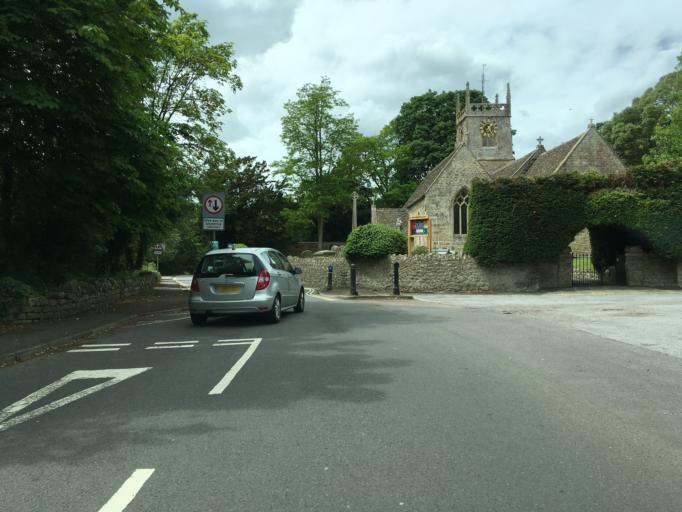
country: GB
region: England
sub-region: Wiltshire
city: Purton
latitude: 51.5727
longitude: -1.8659
